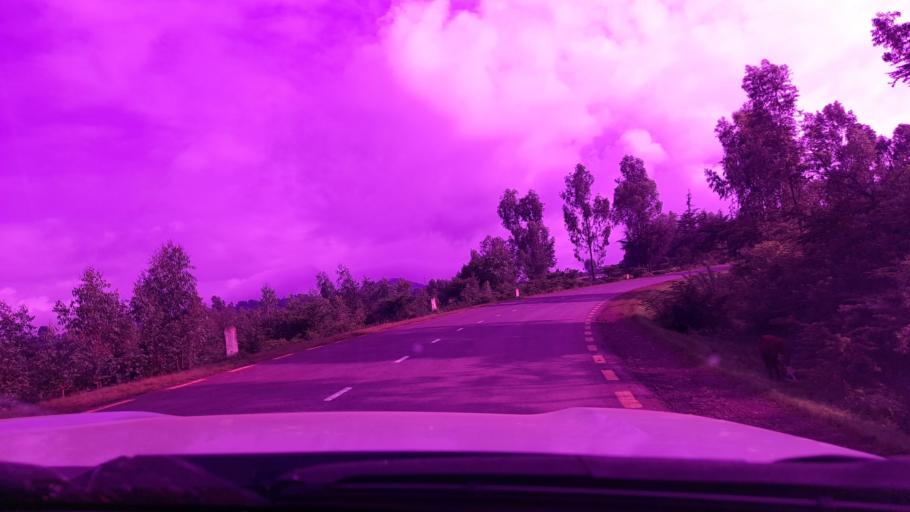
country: ET
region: Oromiya
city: Bedele
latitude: 8.2172
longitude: 36.4445
